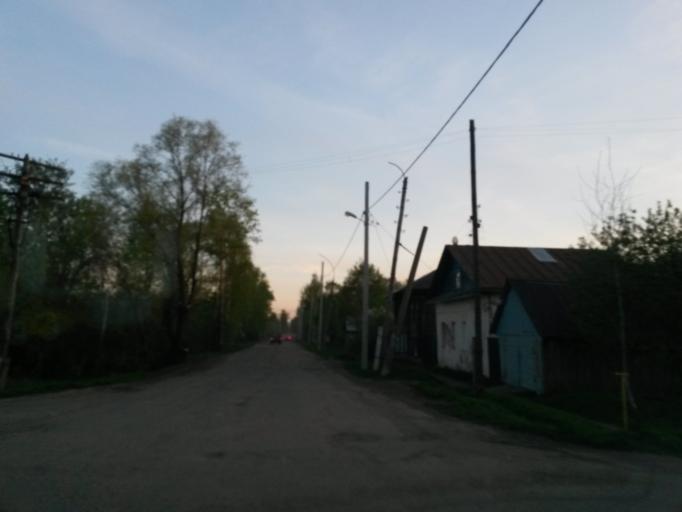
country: RU
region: Jaroslavl
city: Tutayev
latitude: 57.8855
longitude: 39.5492
